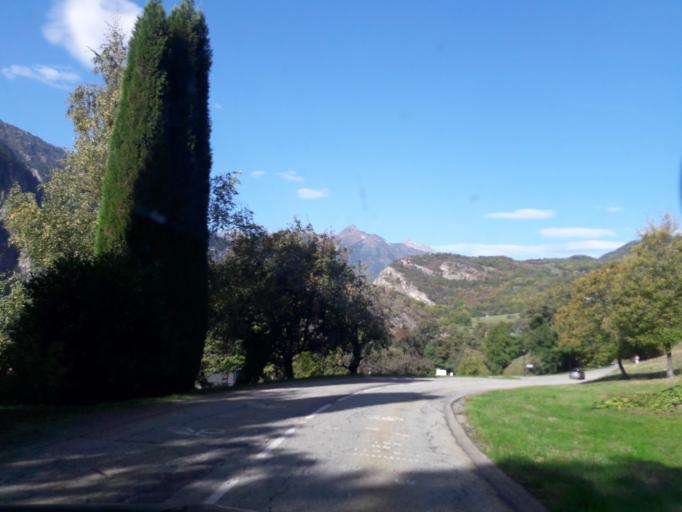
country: FR
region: Rhone-Alpes
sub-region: Departement de la Savoie
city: Saint-Jean-de-Maurienne
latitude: 45.3124
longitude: 6.3526
